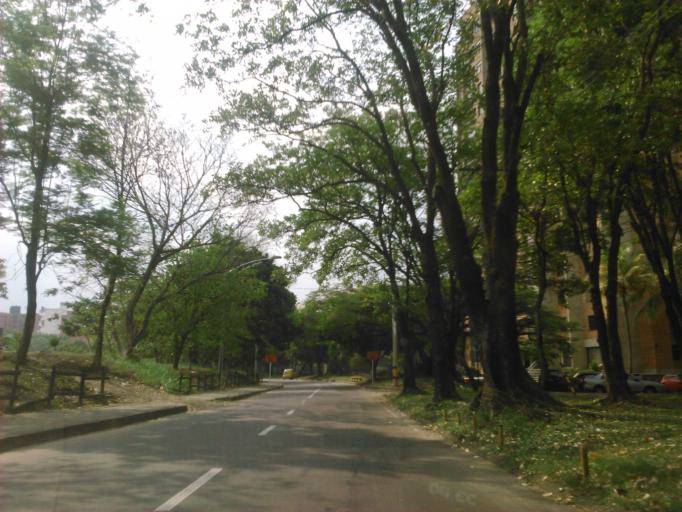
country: CO
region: Antioquia
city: Medellin
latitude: 6.2524
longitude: -75.5807
